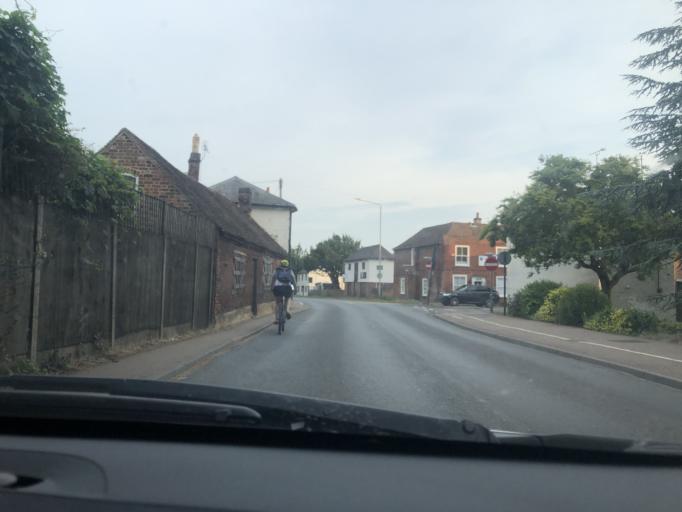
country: GB
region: England
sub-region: Kent
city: Sturry
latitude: 51.3009
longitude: 1.1219
